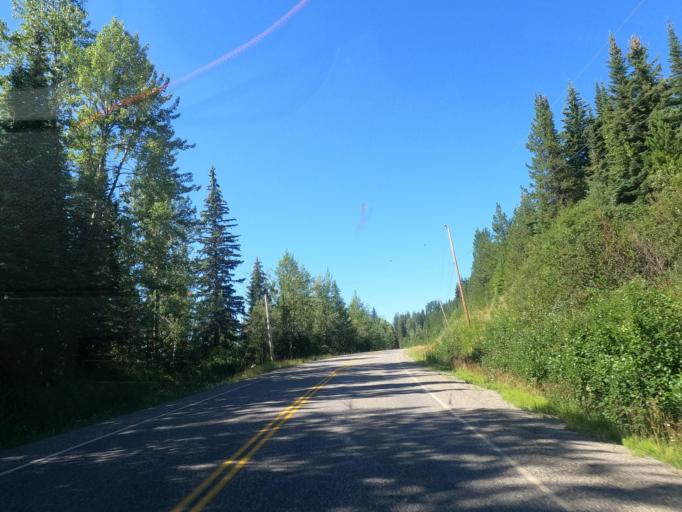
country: CA
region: British Columbia
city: Quesnel
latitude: 53.0345
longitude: -121.9995
